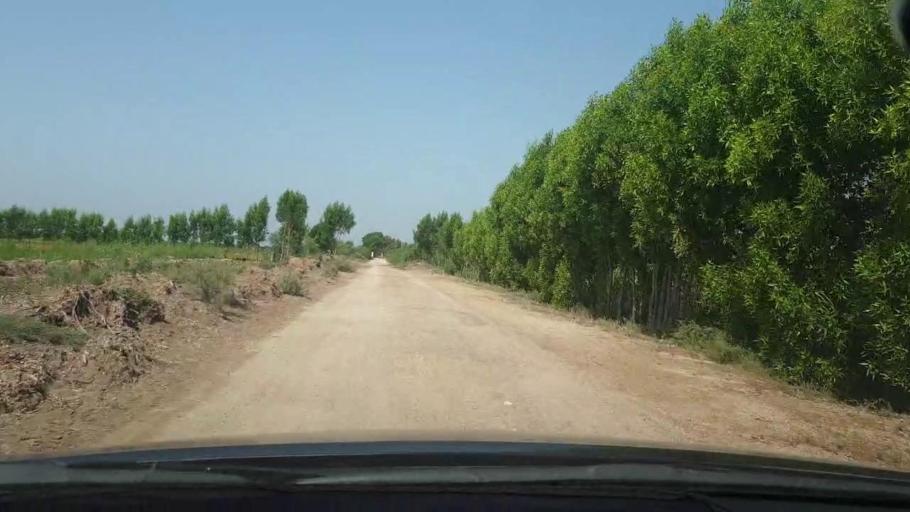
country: PK
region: Sindh
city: Tando Bago
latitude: 24.7194
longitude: 69.0983
